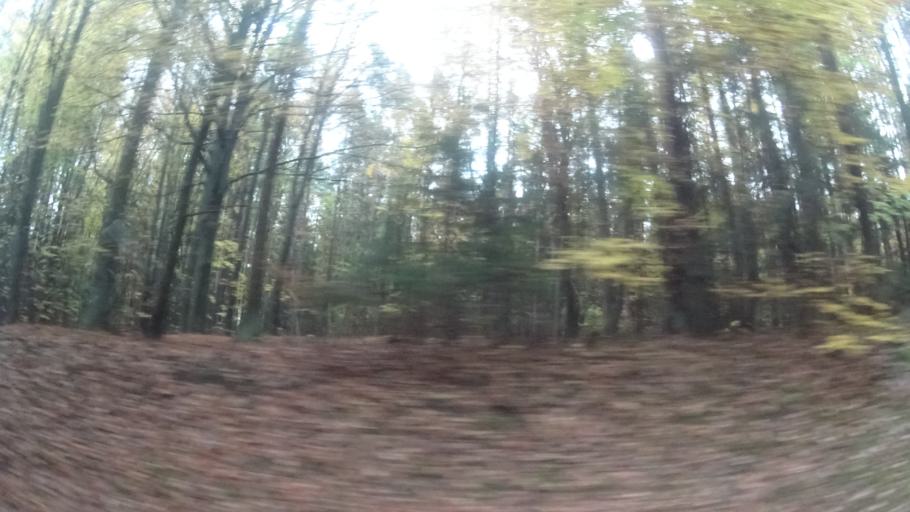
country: DE
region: Bavaria
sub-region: Regierungsbezirk Unterfranken
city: Oberelsbach
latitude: 50.3757
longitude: 10.1014
